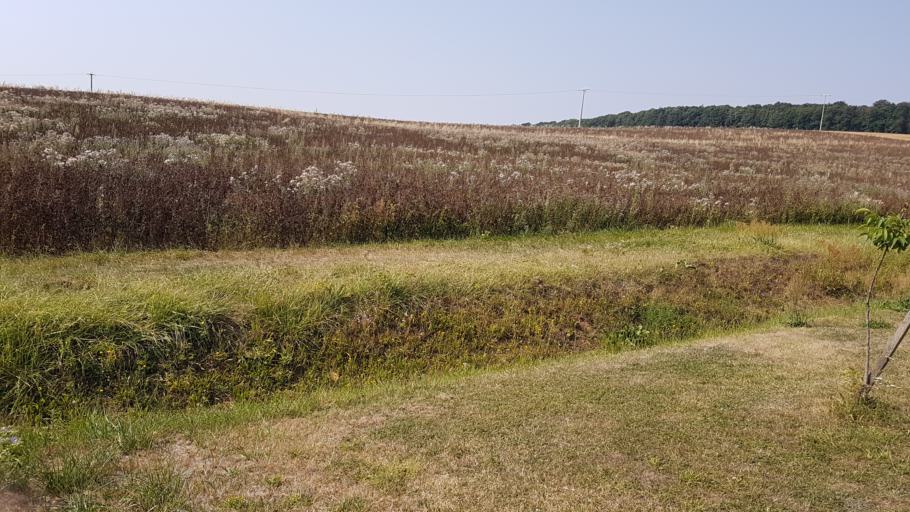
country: DE
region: Bavaria
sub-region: Regierungsbezirk Unterfranken
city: Wasserlosen
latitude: 50.0531
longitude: 9.9966
